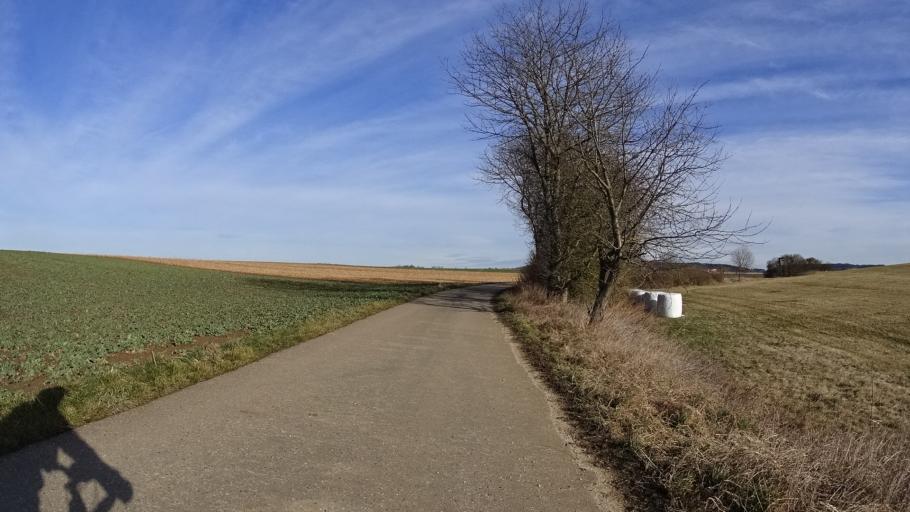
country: DE
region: Bavaria
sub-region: Upper Bavaria
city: Eitensheim
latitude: 48.8220
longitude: 11.3408
